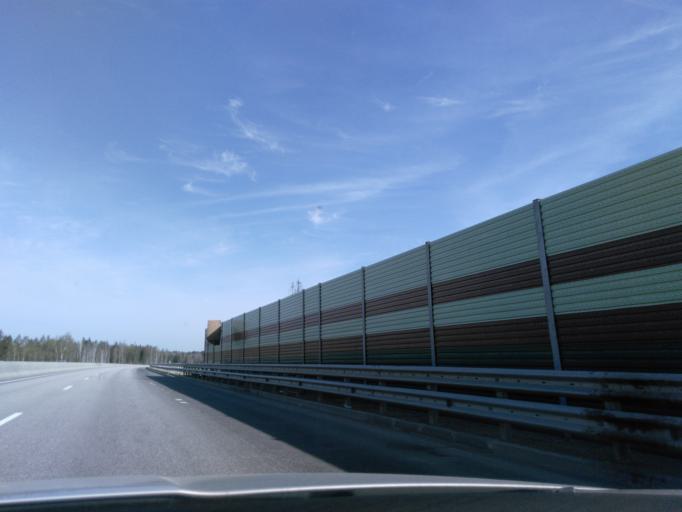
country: RU
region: Moskovskaya
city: Lozhki
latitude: 56.1132
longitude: 37.1213
